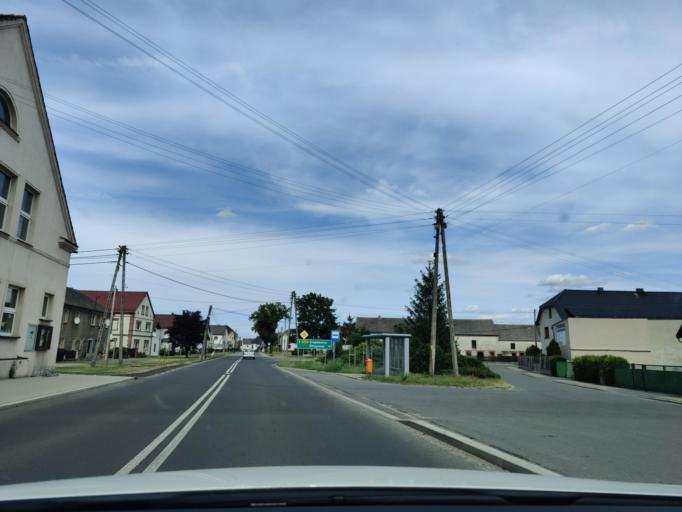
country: PL
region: Opole Voivodeship
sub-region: Powiat krapkowicki
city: Strzeleczki
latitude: 50.4426
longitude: 17.8051
